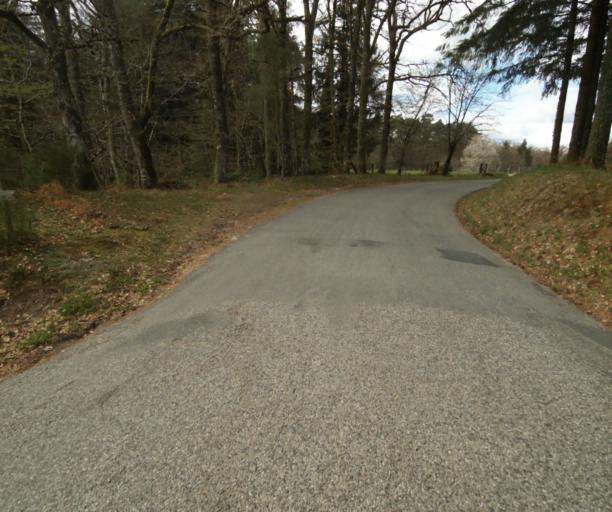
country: FR
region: Limousin
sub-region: Departement de la Correze
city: Argentat
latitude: 45.1889
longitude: 1.9312
